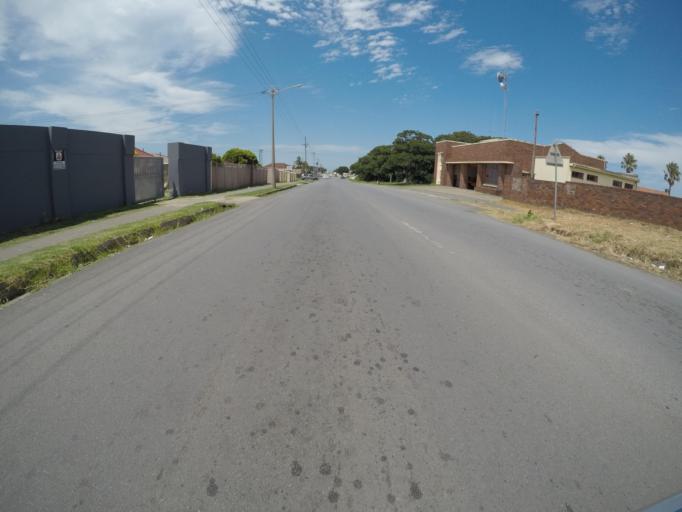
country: ZA
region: Eastern Cape
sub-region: Buffalo City Metropolitan Municipality
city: East London
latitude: -33.0349
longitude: 27.8629
